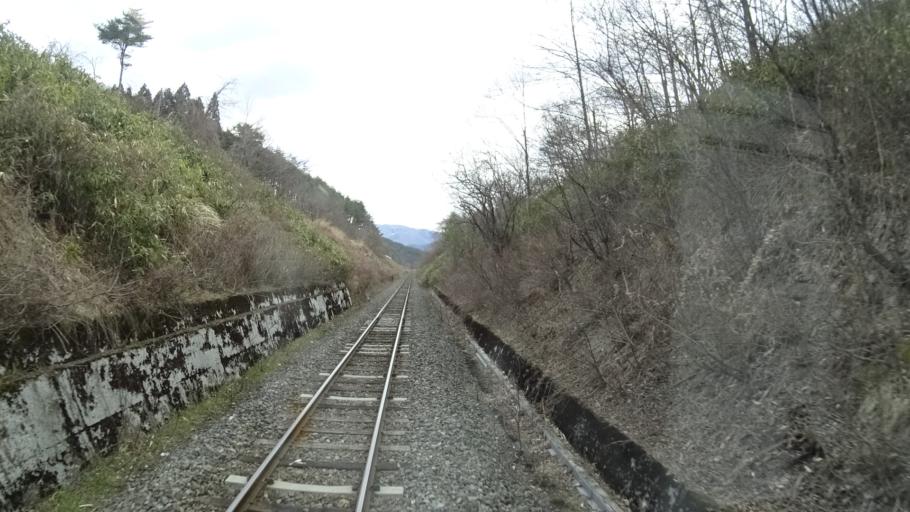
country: JP
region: Iwate
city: Tono
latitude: 39.3218
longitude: 141.3664
